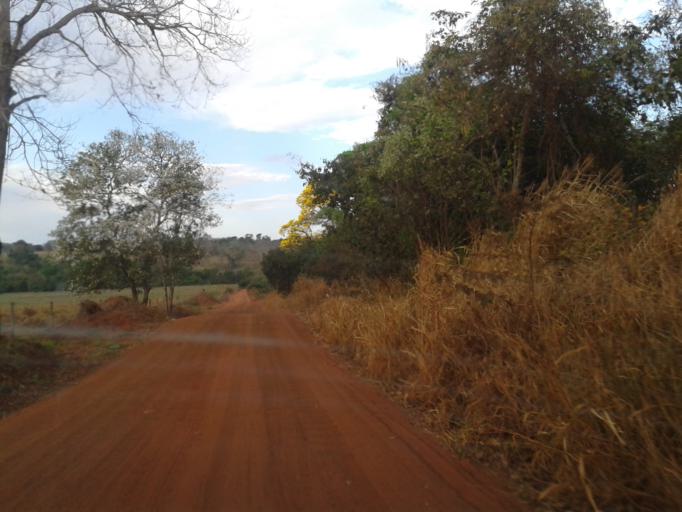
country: BR
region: Minas Gerais
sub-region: Ituiutaba
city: Ituiutaba
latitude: -19.1980
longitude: -49.8301
